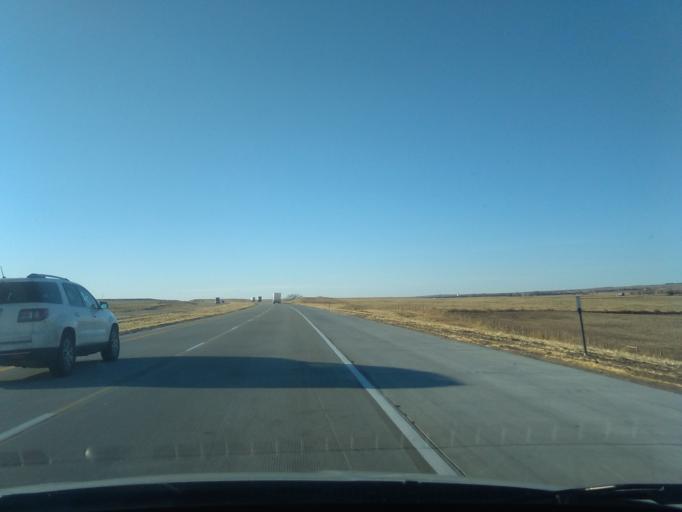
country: US
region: Nebraska
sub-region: Deuel County
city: Chappell
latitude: 41.1106
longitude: -102.5612
